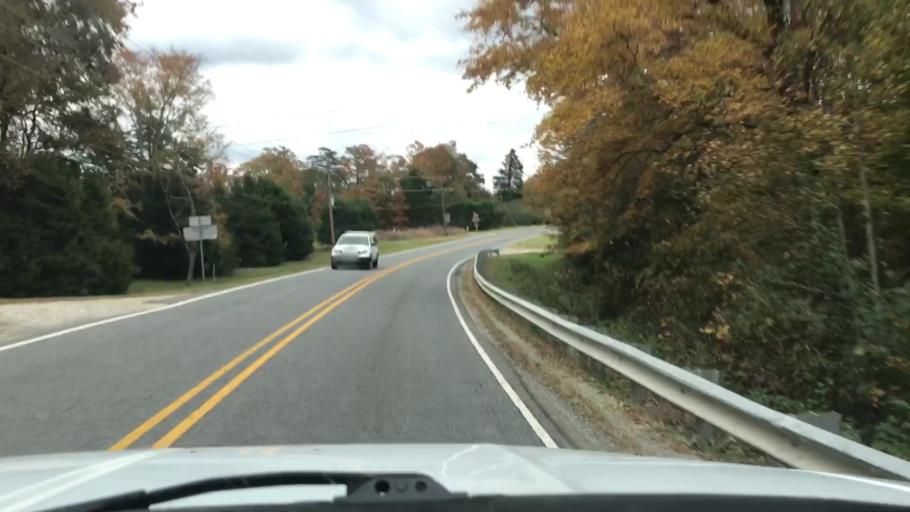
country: US
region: Virginia
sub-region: Goochland County
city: Goochland
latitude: 37.6374
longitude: -77.7961
